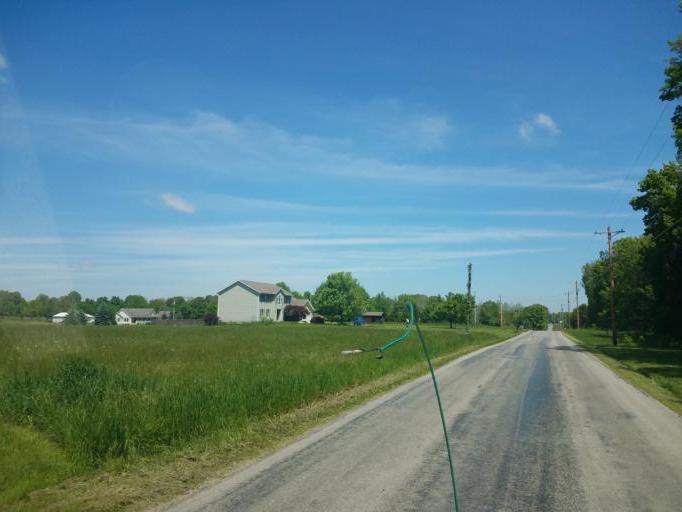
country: US
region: Ohio
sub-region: Ashland County
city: Ashland
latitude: 40.8811
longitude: -82.2497
